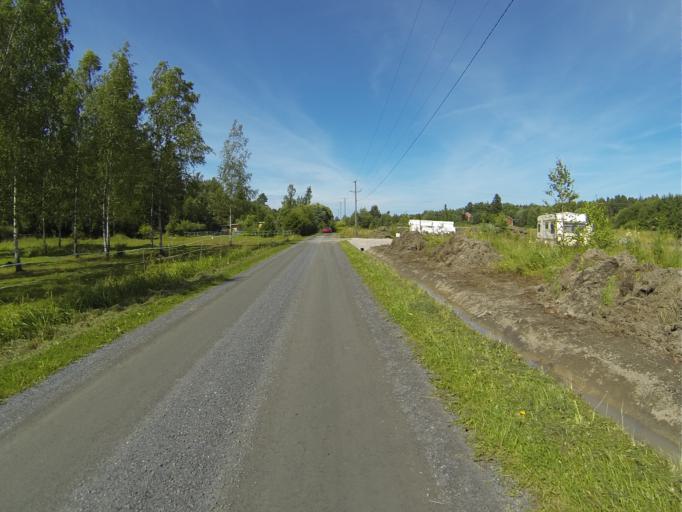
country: FI
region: Varsinais-Suomi
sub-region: Salo
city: Halikko
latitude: 60.2743
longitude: 22.9868
